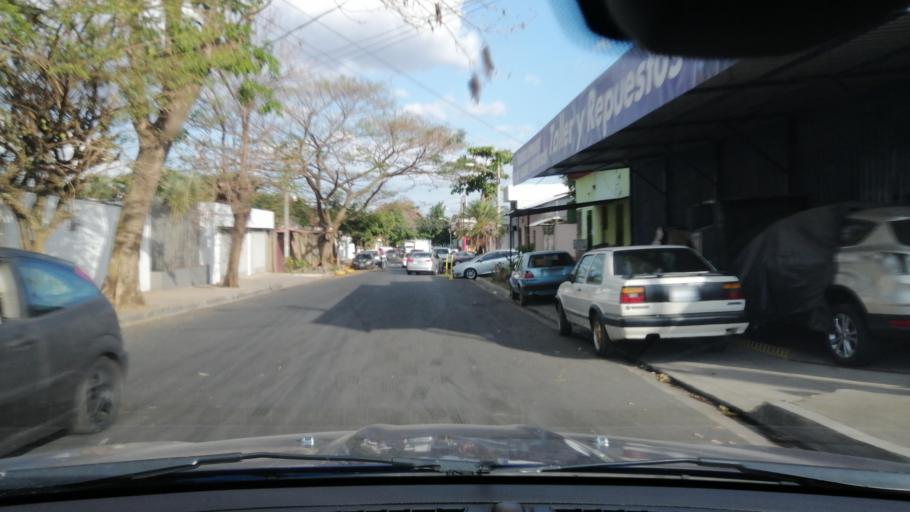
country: SV
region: Santa Ana
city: Santa Ana
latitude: 13.9834
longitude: -89.5599
